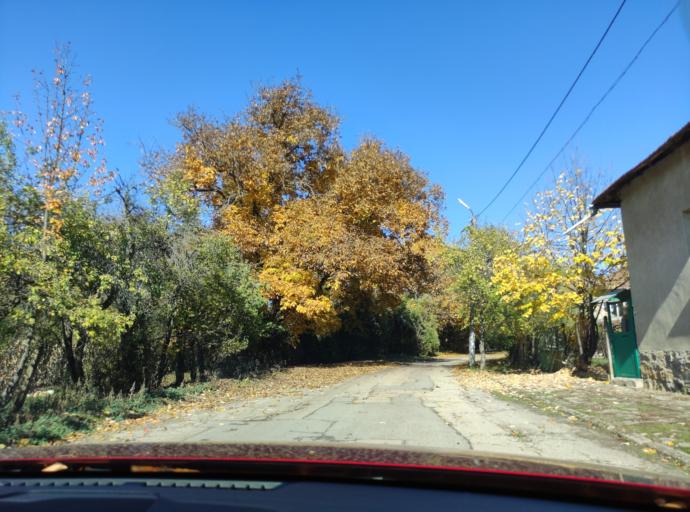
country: BG
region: Montana
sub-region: Obshtina Montana
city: Montana
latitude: 43.4213
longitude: 23.0655
